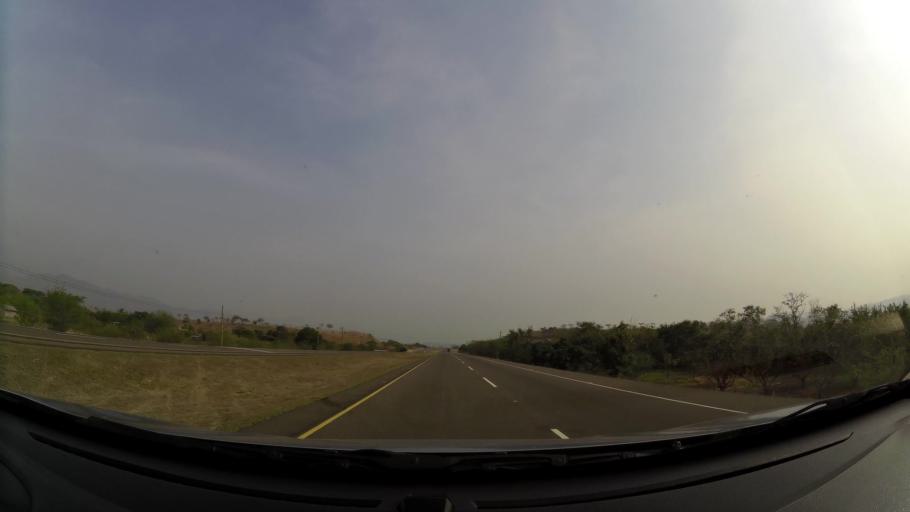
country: HN
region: Comayagua
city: Comayagua
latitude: 14.4460
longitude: -87.6614
